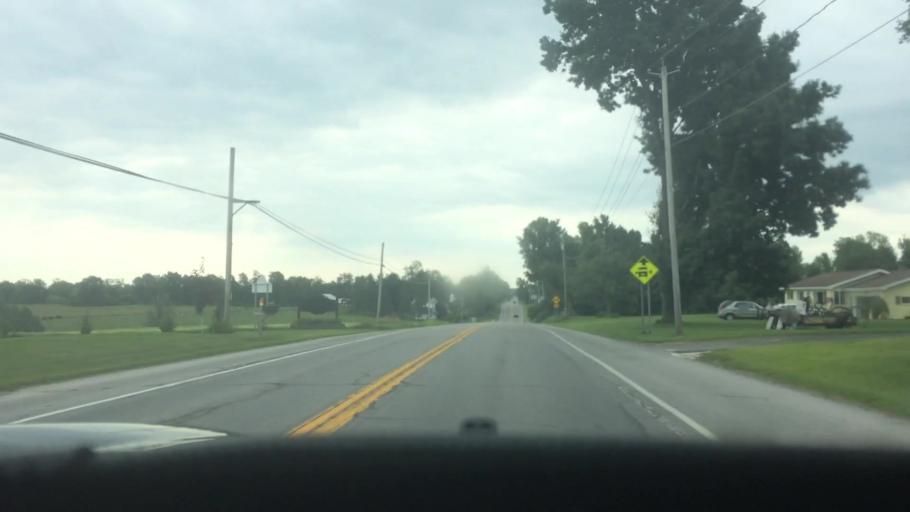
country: US
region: New York
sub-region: St. Lawrence County
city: Ogdensburg
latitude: 44.6130
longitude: -75.4006
